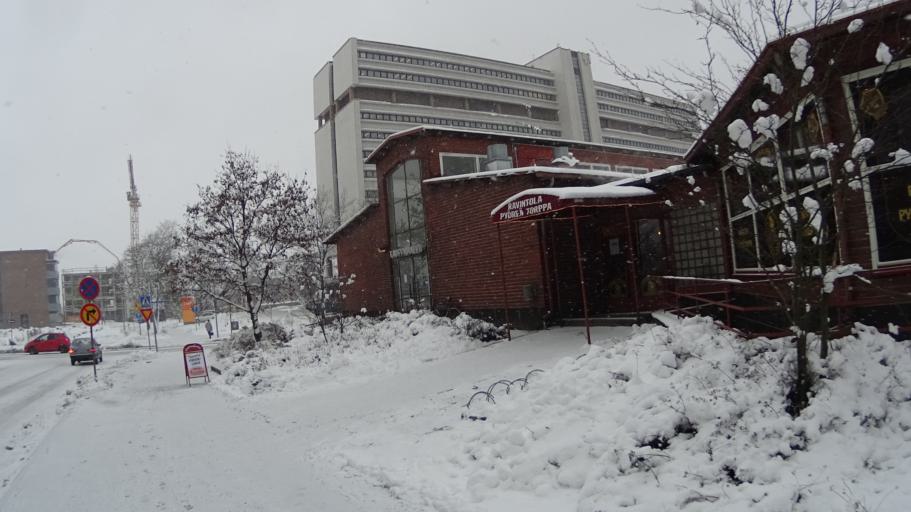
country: FI
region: Kymenlaakso
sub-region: Kouvola
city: Kouvola
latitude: 60.8677
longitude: 26.7009
